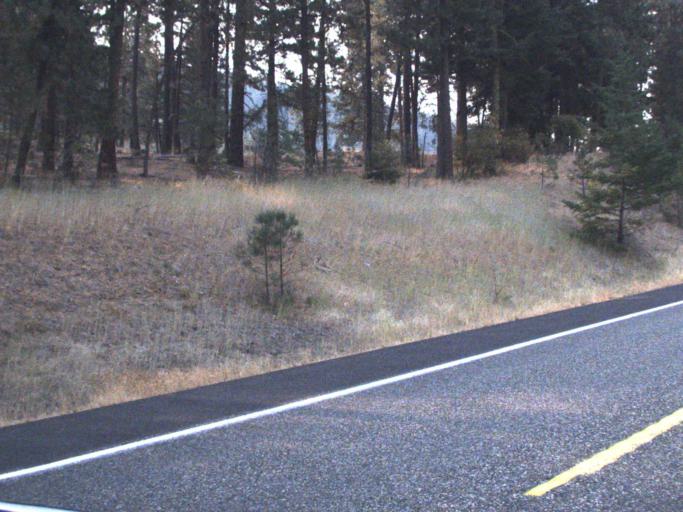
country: US
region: Washington
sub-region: Kittitas County
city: Cle Elum
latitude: 47.1888
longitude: -120.7066
